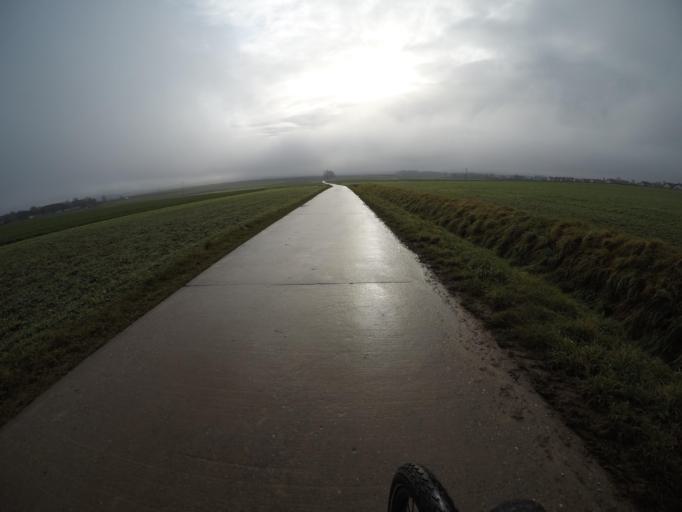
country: DE
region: Baden-Wuerttemberg
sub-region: Regierungsbezirk Stuttgart
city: Wolfschlugen
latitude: 48.6539
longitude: 9.2578
